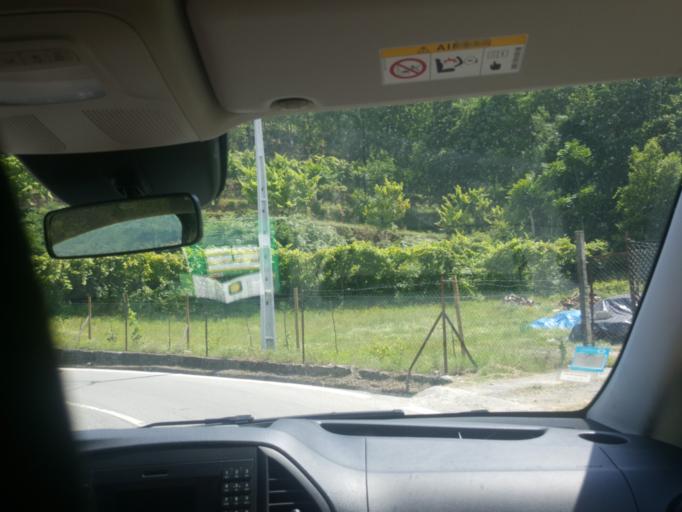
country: PT
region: Porto
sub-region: Amarante
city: Amarante
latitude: 41.2443
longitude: -8.0359
